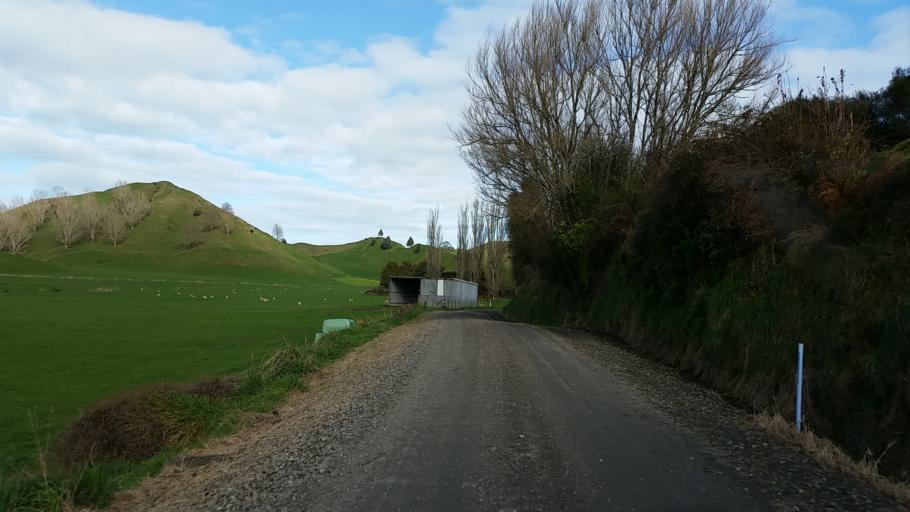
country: NZ
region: Taranaki
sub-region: South Taranaki District
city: Eltham
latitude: -39.2536
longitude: 174.5314
